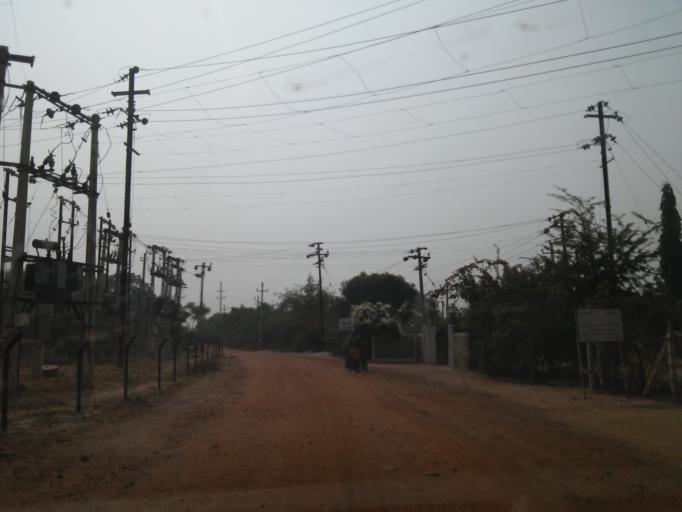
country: IN
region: Gujarat
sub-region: Kachchh
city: Bhuj
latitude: 23.2314
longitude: 69.7400
